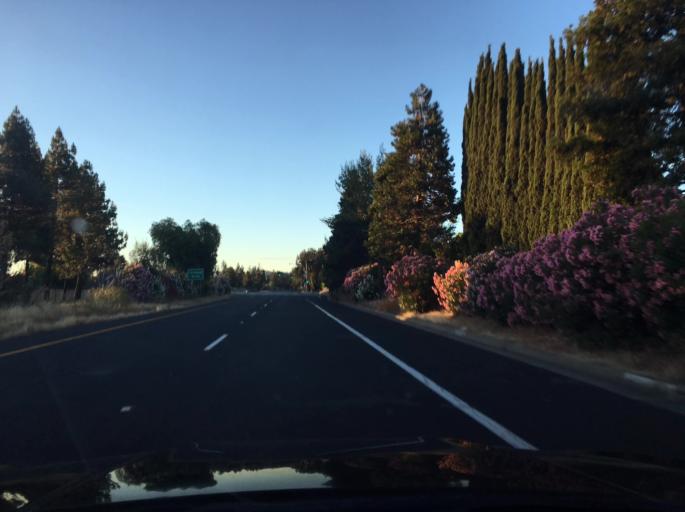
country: US
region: California
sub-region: Santa Clara County
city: Seven Trees
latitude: 37.2169
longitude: -121.8558
